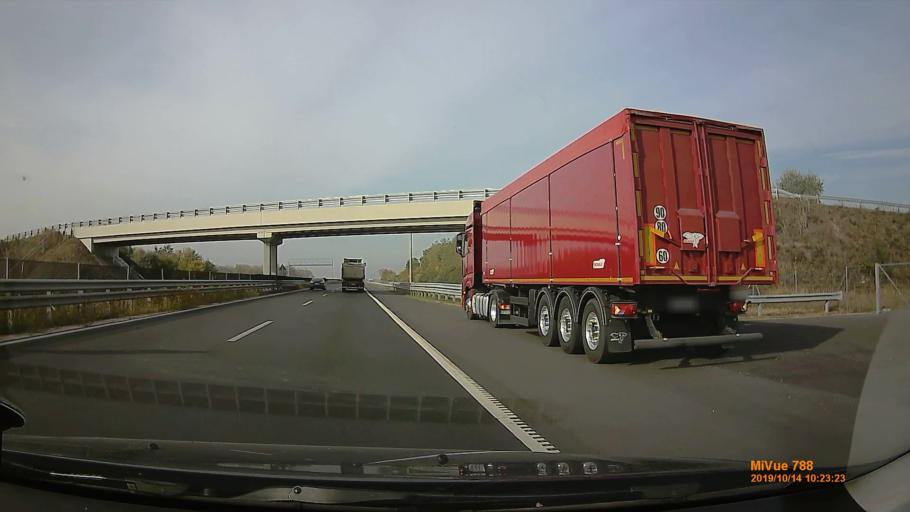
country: HU
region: Pest
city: Tortel
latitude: 47.1905
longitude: 19.8996
